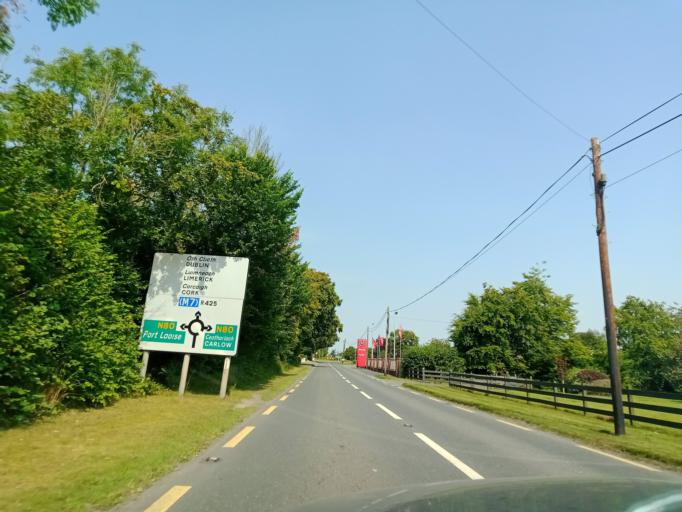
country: IE
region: Leinster
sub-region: Laois
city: Portlaoise
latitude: 53.0295
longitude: -7.2624
